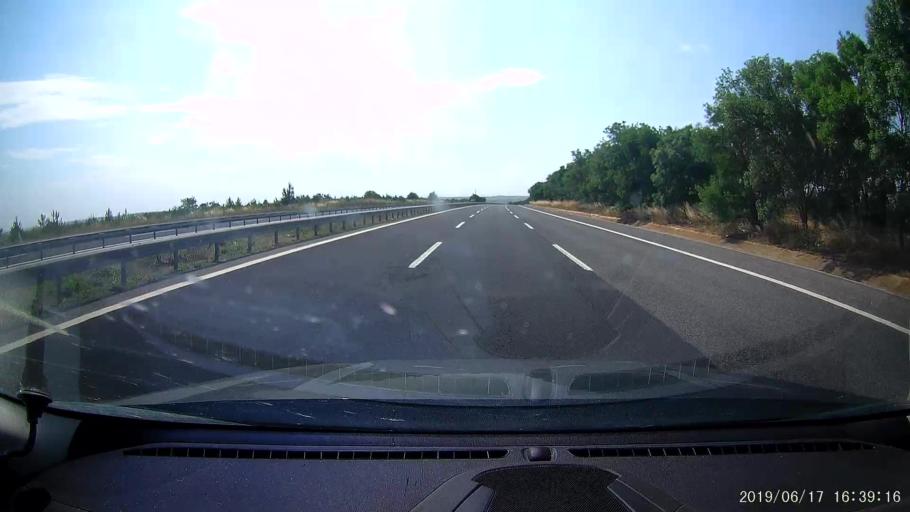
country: TR
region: Kirklareli
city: Luleburgaz
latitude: 41.4478
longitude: 27.4161
